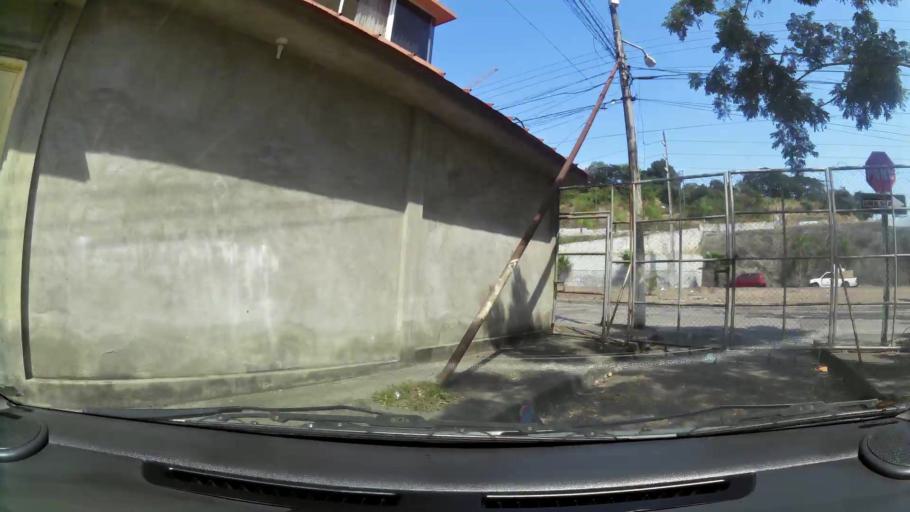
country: EC
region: Guayas
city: Eloy Alfaro
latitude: -2.1335
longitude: -79.9137
